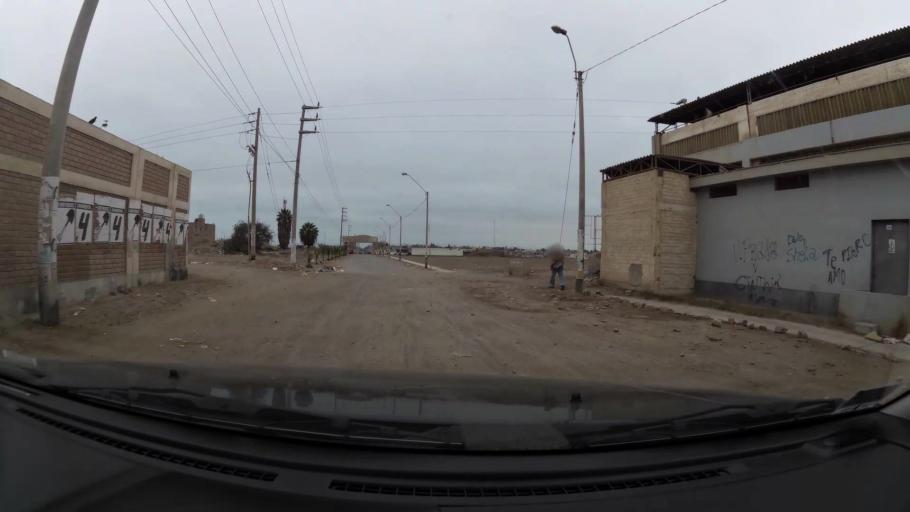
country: PE
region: Ica
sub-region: Provincia de Pisco
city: Pisco
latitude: -13.7088
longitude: -76.1968
